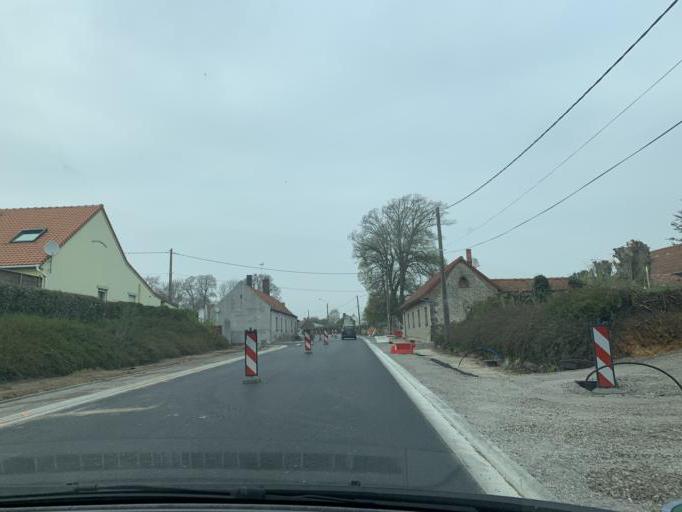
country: FR
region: Nord-Pas-de-Calais
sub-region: Departement du Pas-de-Calais
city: Montreuil
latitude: 50.4156
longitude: 1.7265
